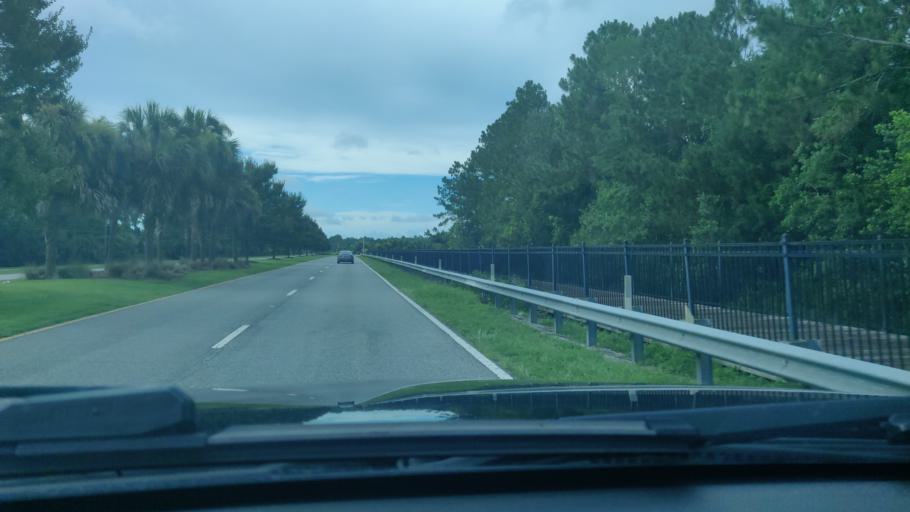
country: US
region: Florida
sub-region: Flagler County
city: Palm Coast
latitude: 29.5268
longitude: -81.2255
